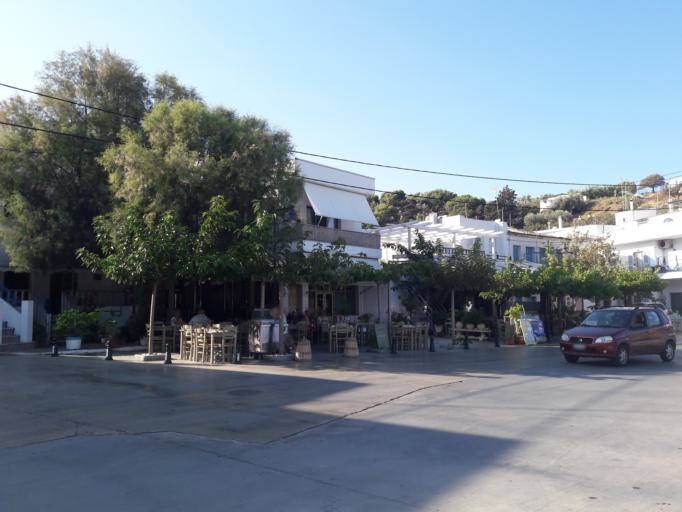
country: GR
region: Central Greece
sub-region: Nomos Evvoias
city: Skyros
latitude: 38.8422
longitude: 24.5374
